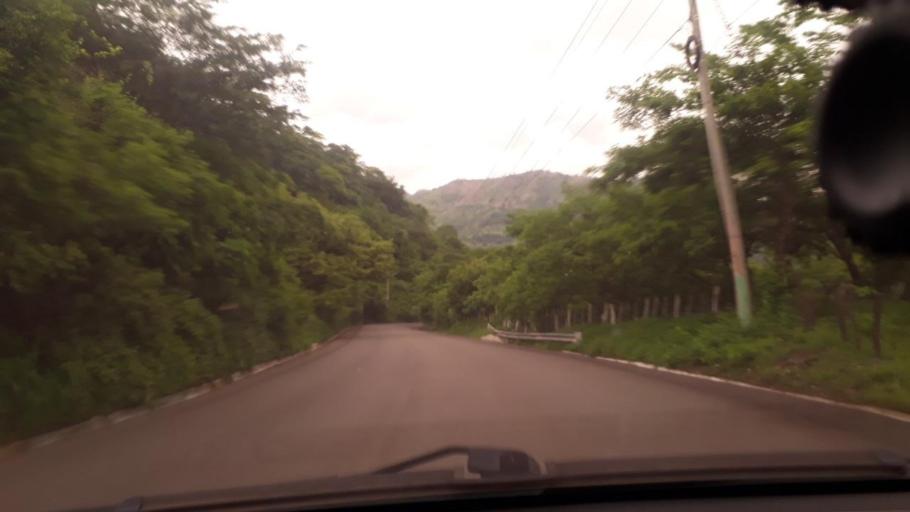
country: GT
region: Chiquimula
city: San Jacinto
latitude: 14.7346
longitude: -89.4985
